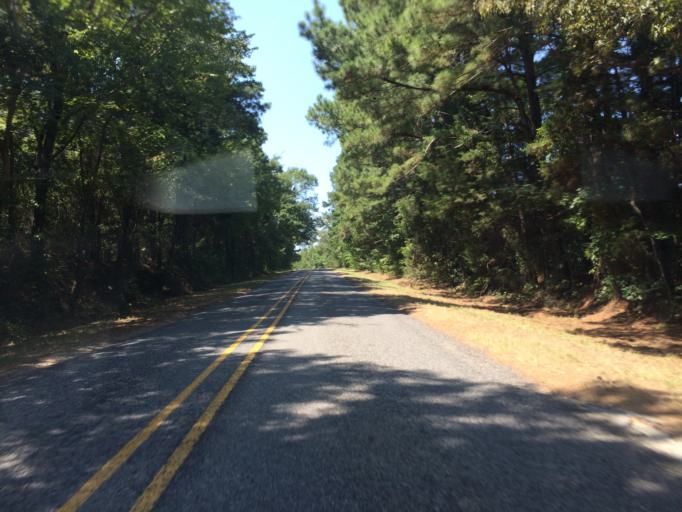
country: US
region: Texas
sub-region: Wood County
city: Hawkins
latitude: 32.7420
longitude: -95.2680
